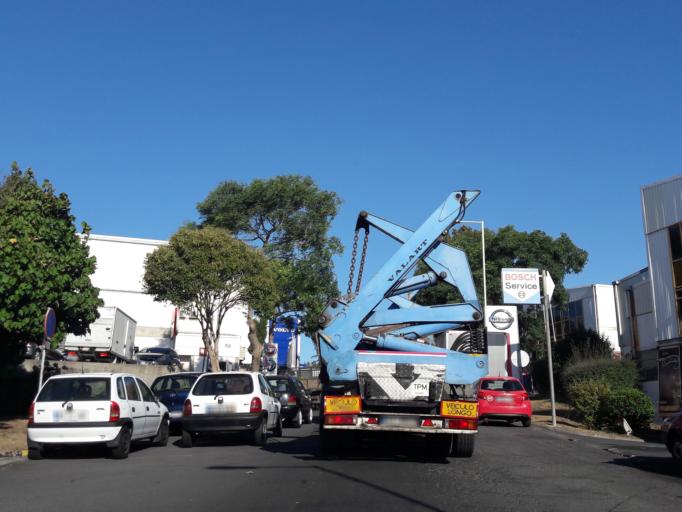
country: PT
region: Madeira
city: Canico
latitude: 32.6501
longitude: -16.8581
